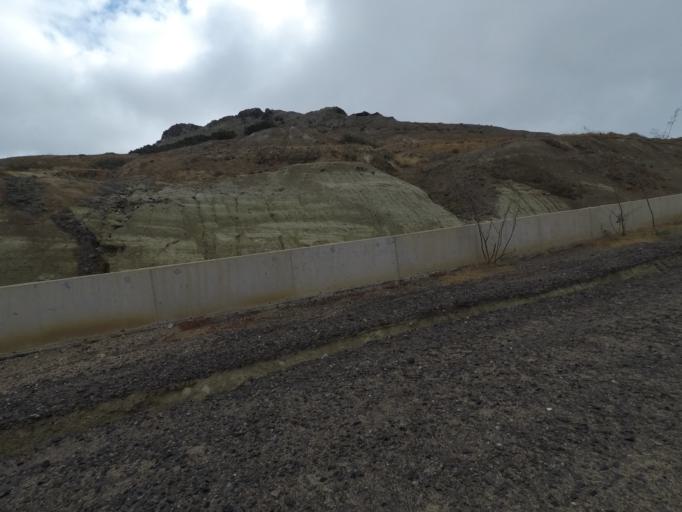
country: PT
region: Madeira
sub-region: Porto Santo
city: Vila de Porto Santo
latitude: 33.0470
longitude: -16.3647
